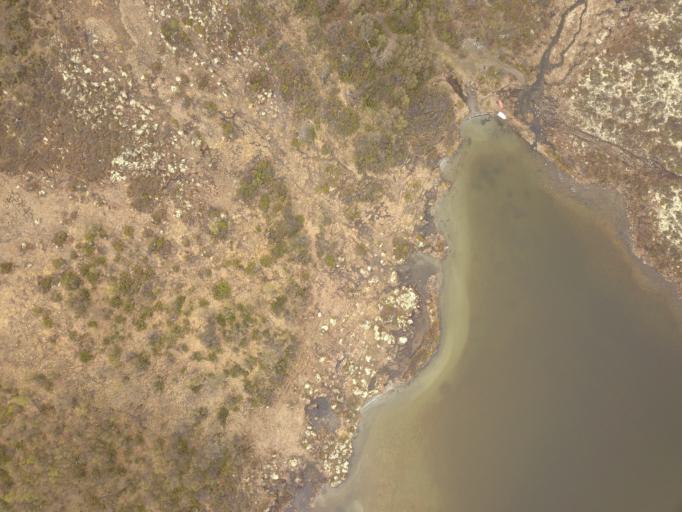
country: NO
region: Hedmark
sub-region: Folldal
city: Folldal
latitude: 62.2300
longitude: 9.6450
